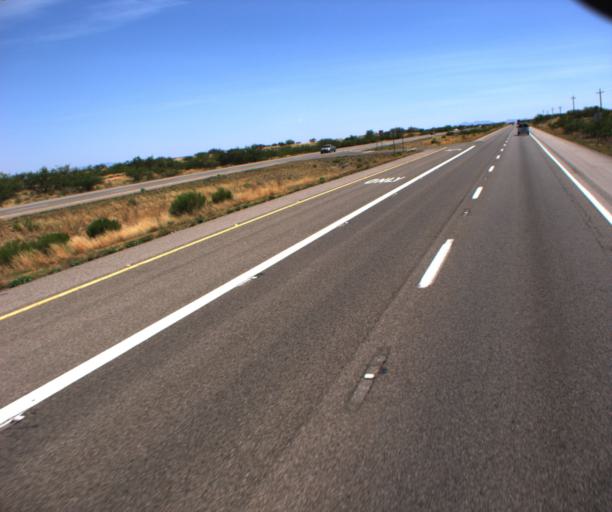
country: US
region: Arizona
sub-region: Cochise County
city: Whetstone
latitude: 31.9148
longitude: -110.3414
